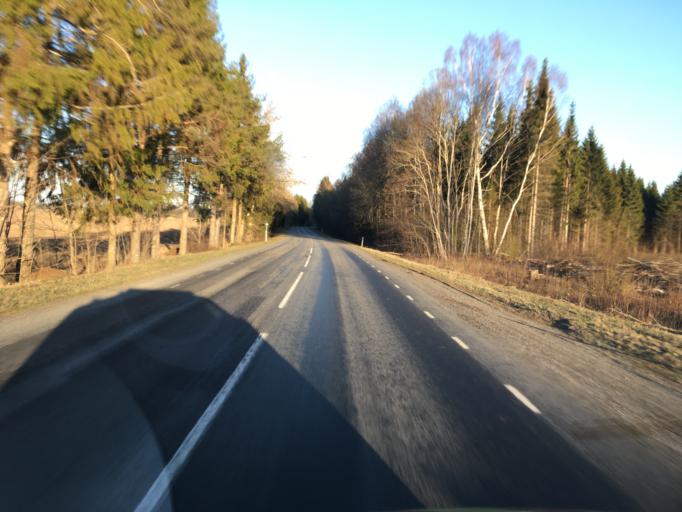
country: EE
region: Raplamaa
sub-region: Rapla vald
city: Rapla
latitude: 59.0679
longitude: 24.9168
